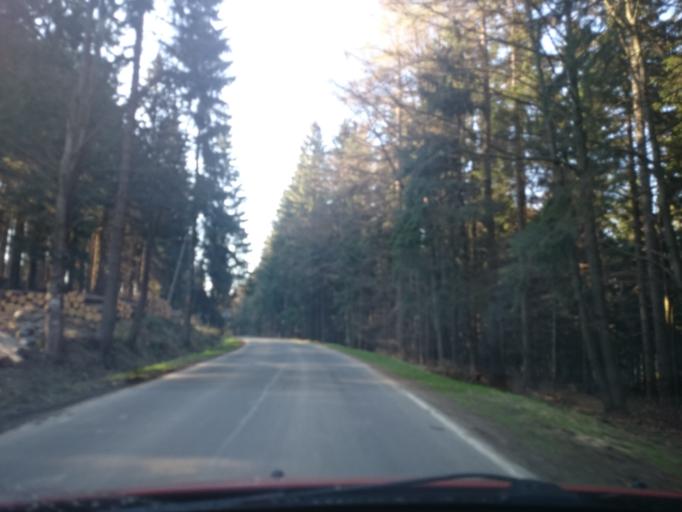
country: PL
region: Lower Silesian Voivodeship
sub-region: Powiat klodzki
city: Duszniki-Zdroj
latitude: 50.3260
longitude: 16.4113
